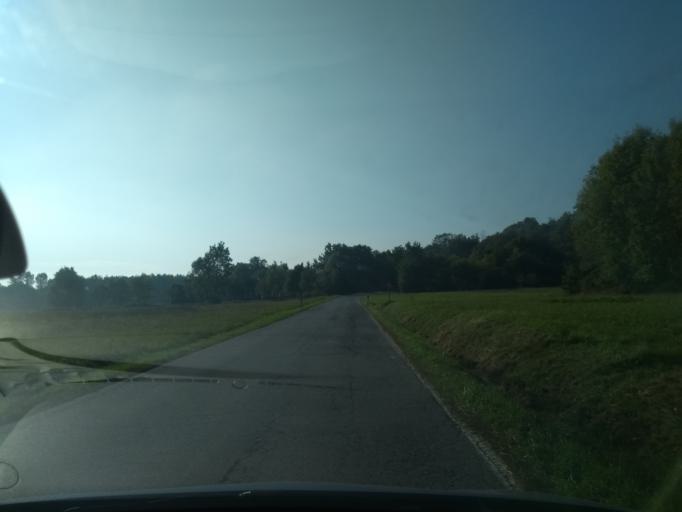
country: IT
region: Piedmont
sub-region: Provincia di Torino
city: Monasterolo
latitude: 45.2399
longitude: 7.5118
